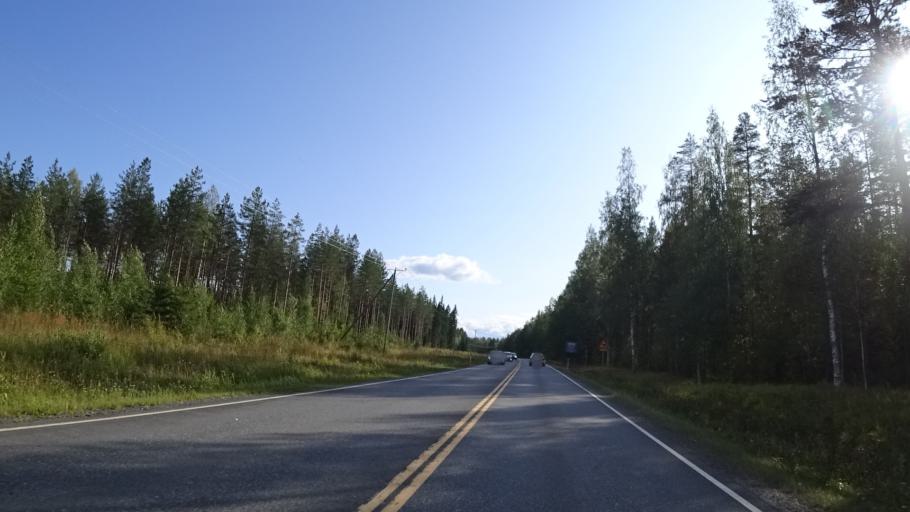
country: FI
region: North Karelia
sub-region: Keski-Karjala
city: Kesaelahti
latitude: 62.0567
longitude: 29.9048
